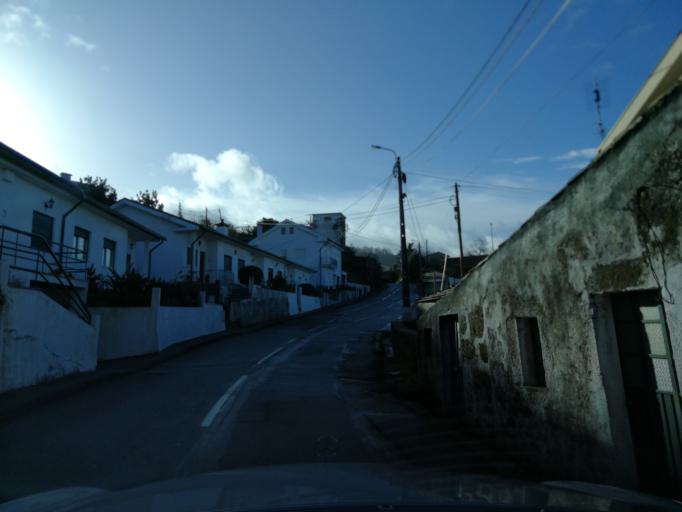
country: PT
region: Braga
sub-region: Braga
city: Braga
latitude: 41.5503
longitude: -8.3886
